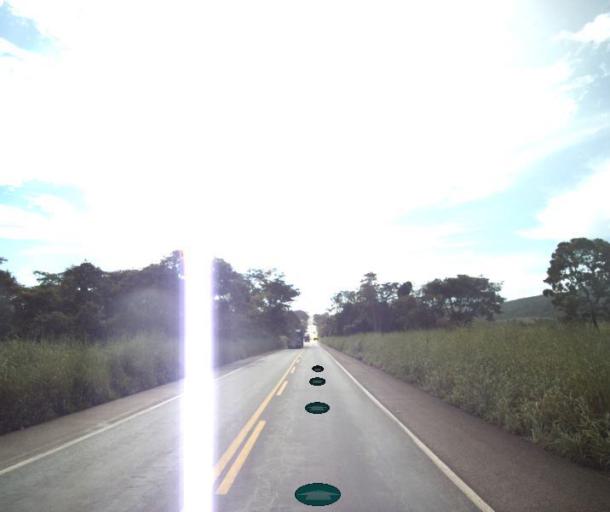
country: BR
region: Goias
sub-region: Jaragua
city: Jaragua
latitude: -15.6322
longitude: -49.3790
